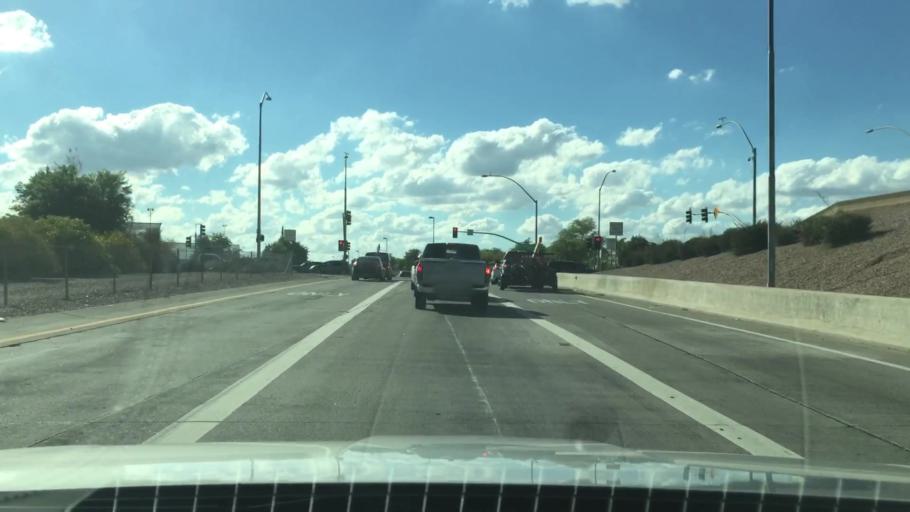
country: US
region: Arizona
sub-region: Maricopa County
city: Mesa
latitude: 33.3866
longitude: -111.8220
